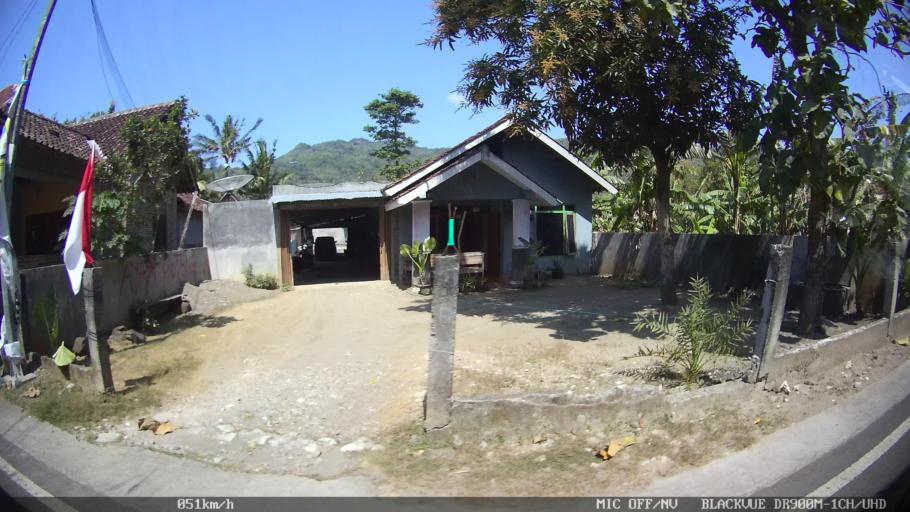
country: ID
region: Daerah Istimewa Yogyakarta
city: Pundong
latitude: -7.9678
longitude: 110.3531
